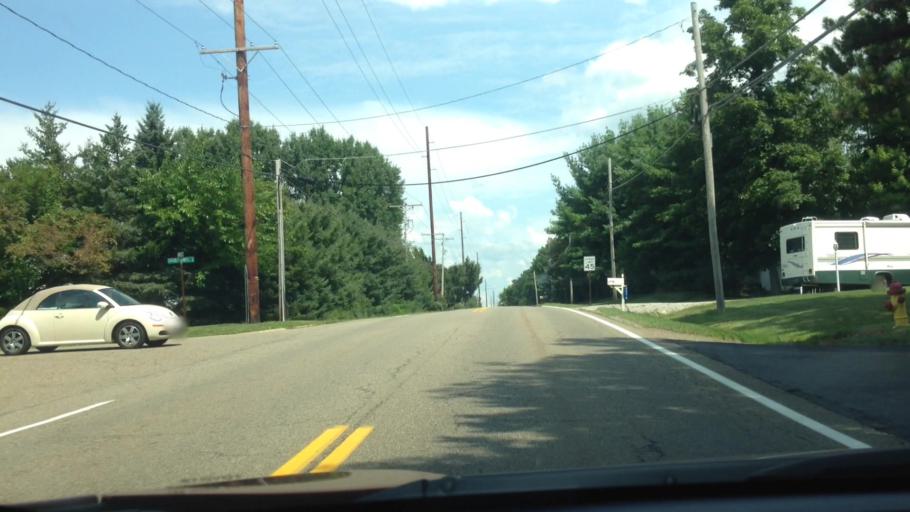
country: US
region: Ohio
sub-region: Stark County
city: Massillon
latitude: 40.8430
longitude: -81.5116
